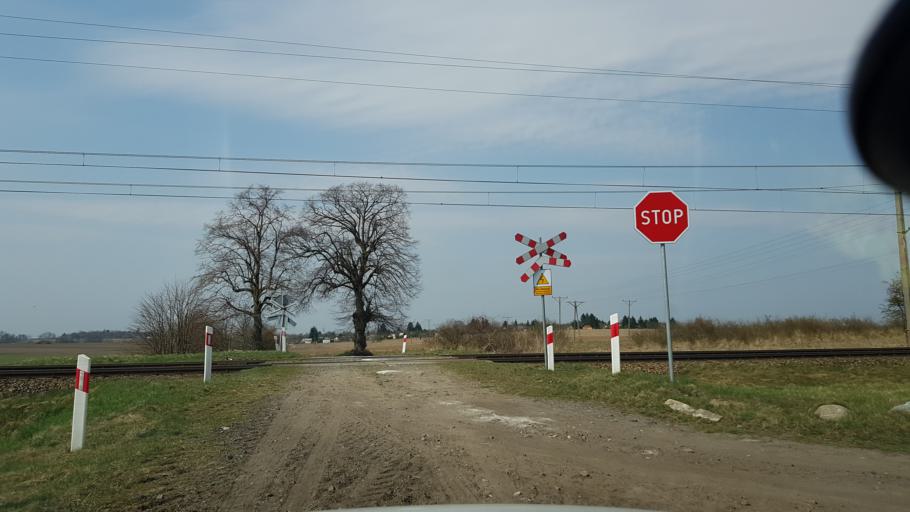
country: PL
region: West Pomeranian Voivodeship
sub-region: Powiat stargardzki
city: Stargard Szczecinski
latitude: 53.3338
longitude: 15.0816
